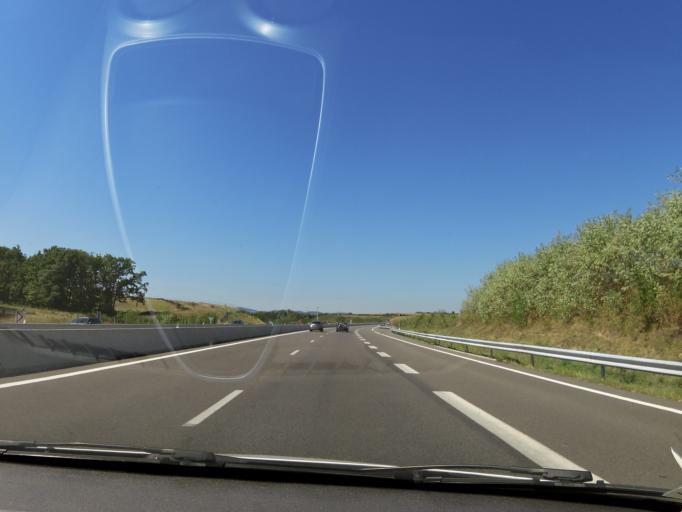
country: FR
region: Rhone-Alpes
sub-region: Departement du Rhone
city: Lozanne
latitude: 45.8538
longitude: 4.6568
